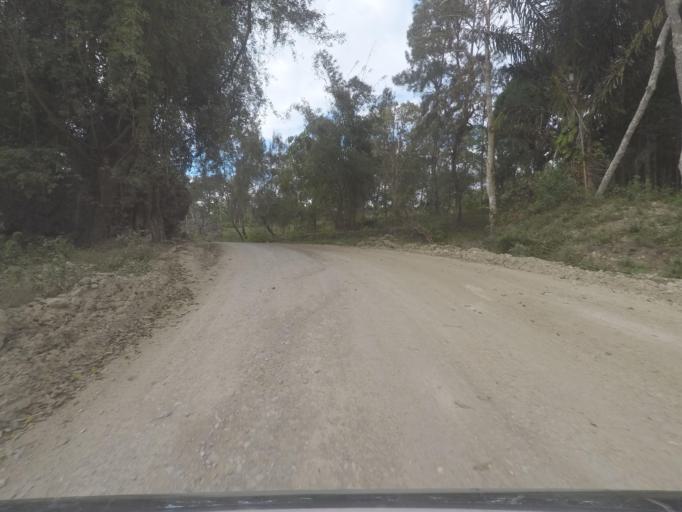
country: TL
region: Baucau
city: Venilale
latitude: -8.6250
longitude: 126.3825
